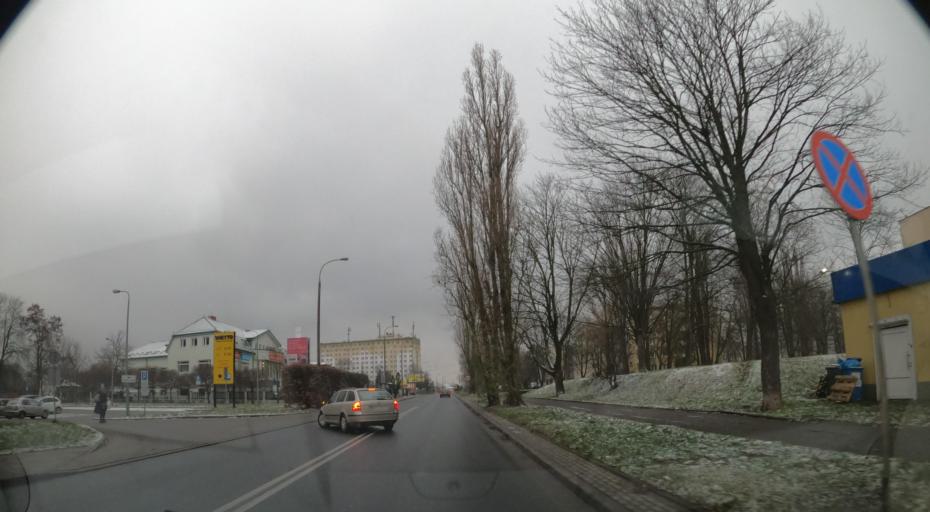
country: PL
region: Masovian Voivodeship
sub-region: Plock
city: Plock
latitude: 52.5516
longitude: 19.6761
